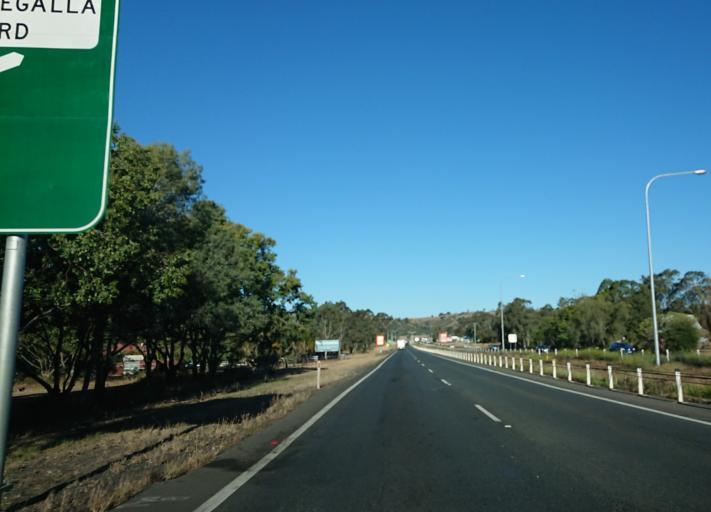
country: AU
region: Queensland
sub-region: Ipswich
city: Thagoona
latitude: -27.5528
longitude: 152.5388
